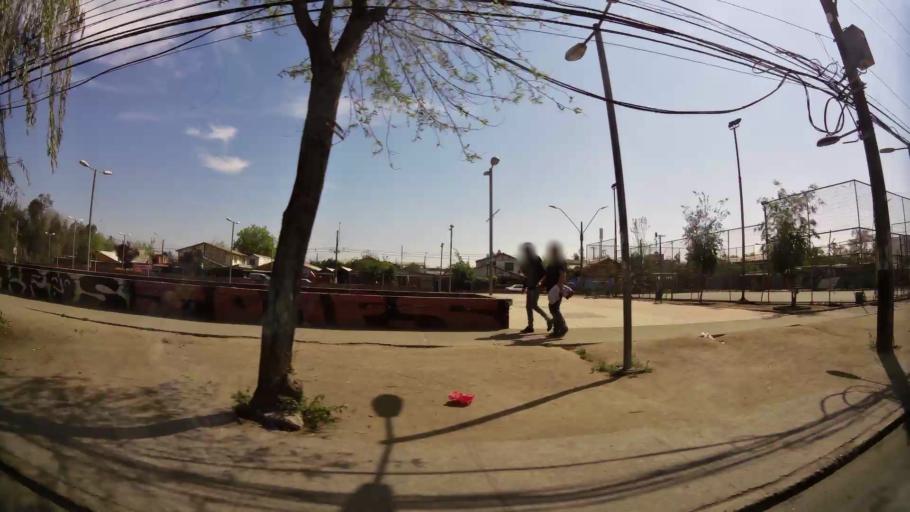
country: CL
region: Santiago Metropolitan
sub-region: Provincia de Santiago
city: Lo Prado
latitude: -33.4728
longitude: -70.7216
